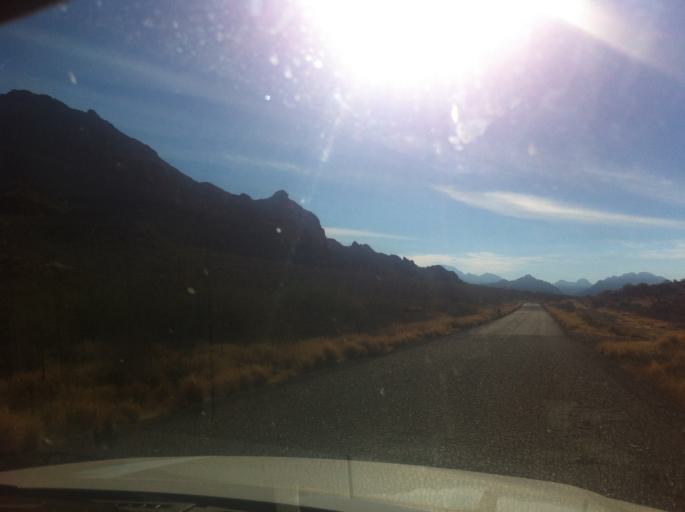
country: MX
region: Sonora
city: Heroica Guaymas
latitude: 27.9452
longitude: -110.9750
